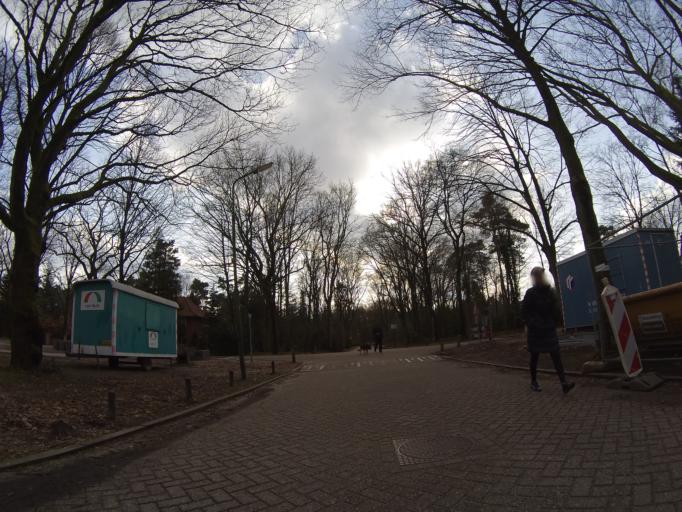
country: NL
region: Utrecht
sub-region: Gemeente Soest
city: Soest
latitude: 52.1590
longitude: 5.2990
